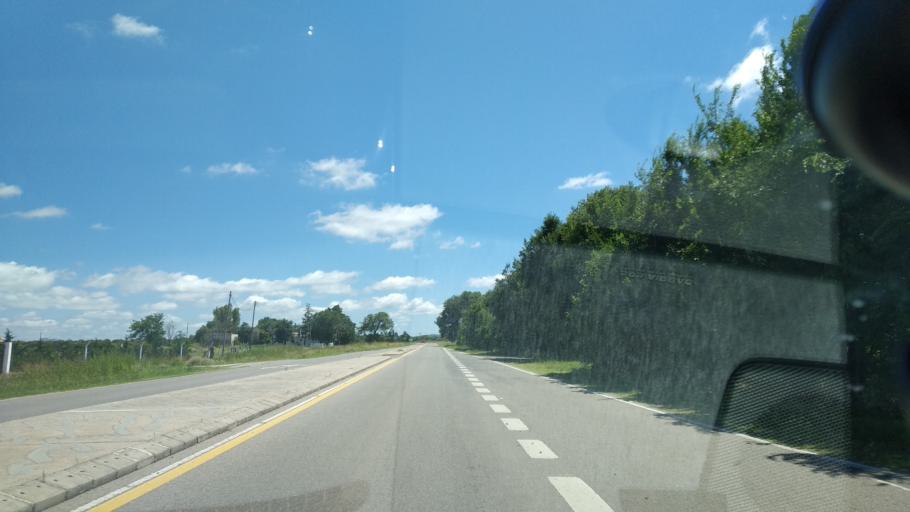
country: AR
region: Cordoba
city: Salsacate
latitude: -31.4966
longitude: -65.1085
